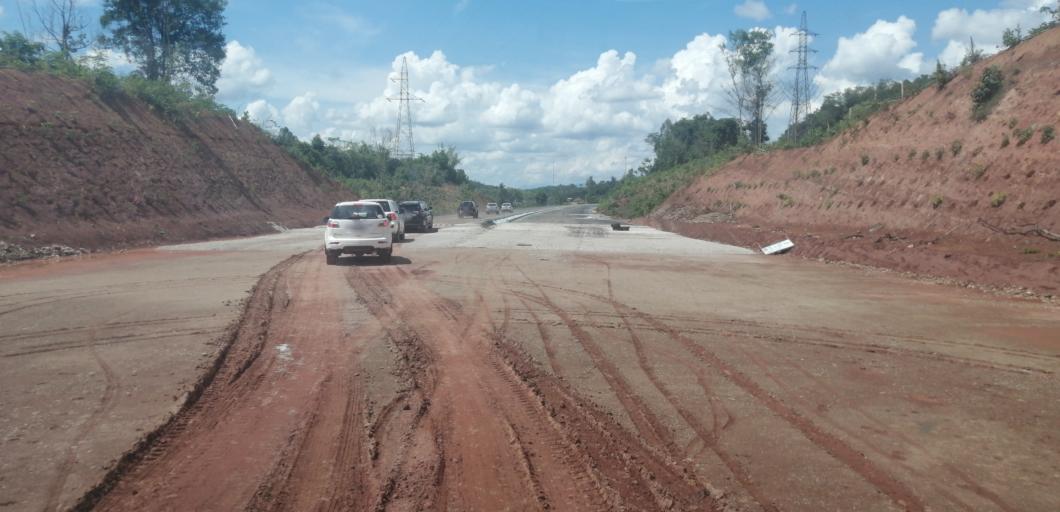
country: LA
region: Vientiane
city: Muang Phon-Hong
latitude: 18.6838
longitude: 102.3392
